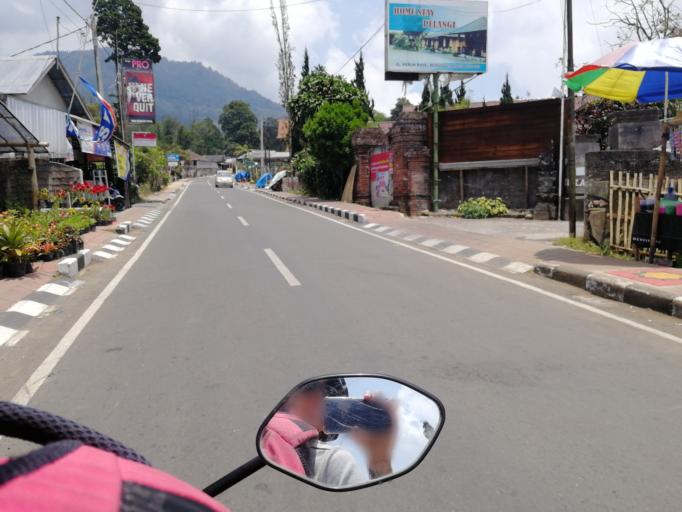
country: ID
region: Bali
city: Munduk
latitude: -8.2834
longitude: 115.1581
